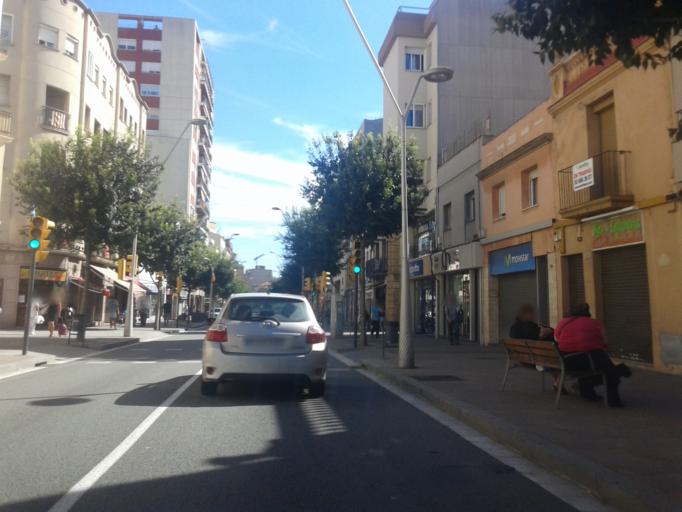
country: ES
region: Catalonia
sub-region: Provincia de Barcelona
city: Sant Feliu de Llobregat
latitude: 41.3822
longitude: 2.0427
